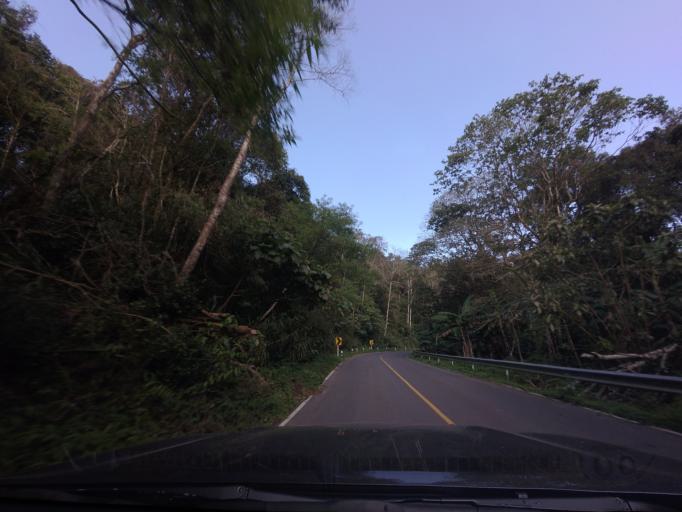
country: TH
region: Phetchabun
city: Lom Kao
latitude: 16.9324
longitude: 101.0701
